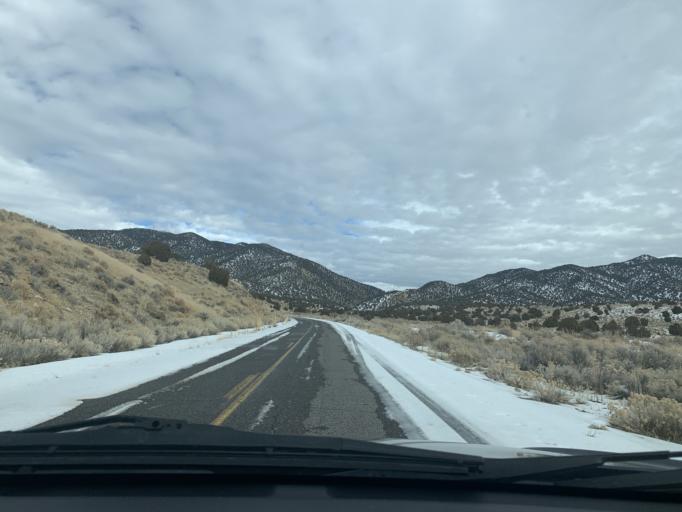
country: US
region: Utah
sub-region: Tooele County
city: Tooele
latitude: 40.3018
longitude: -112.2669
